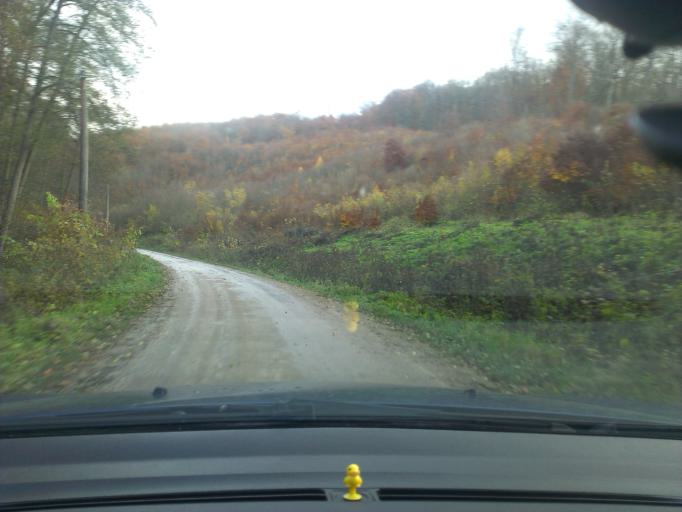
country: SK
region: Trnavsky
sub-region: Okres Trnava
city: Piestany
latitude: 48.6072
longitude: 17.8963
